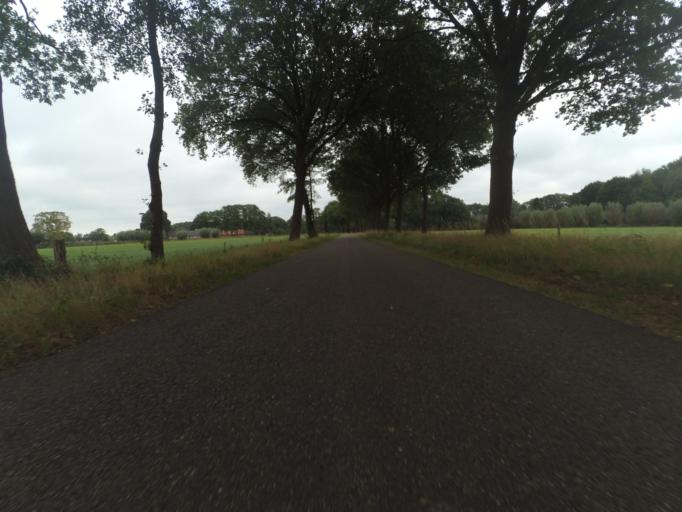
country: NL
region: Utrecht
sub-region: Gemeente Utrechtse Heuvelrug
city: Overberg
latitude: 52.0717
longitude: 5.4866
